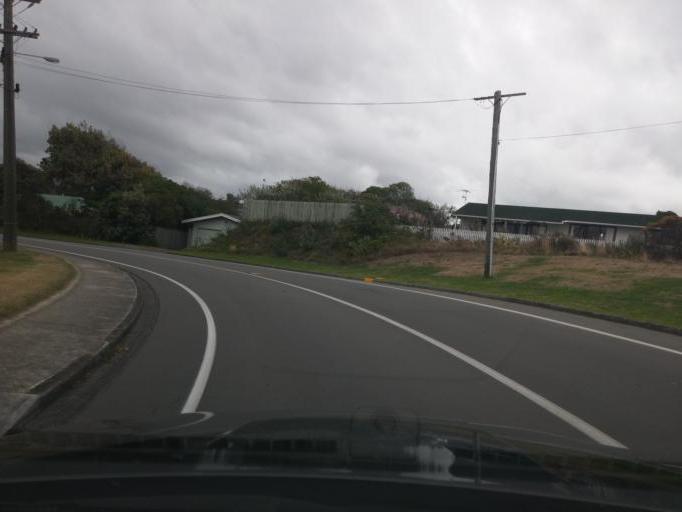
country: NZ
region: Wellington
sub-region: Kapiti Coast District
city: Paraparaumu
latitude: -40.8602
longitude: 175.0288
